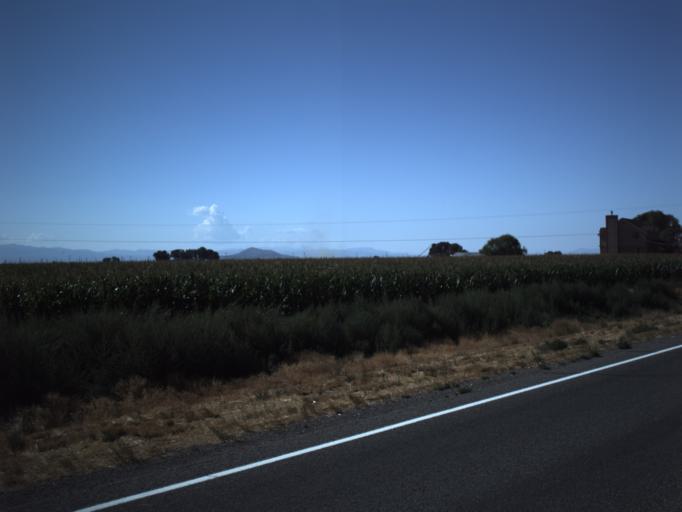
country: US
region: Utah
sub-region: Millard County
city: Delta
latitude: 39.3390
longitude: -112.6056
